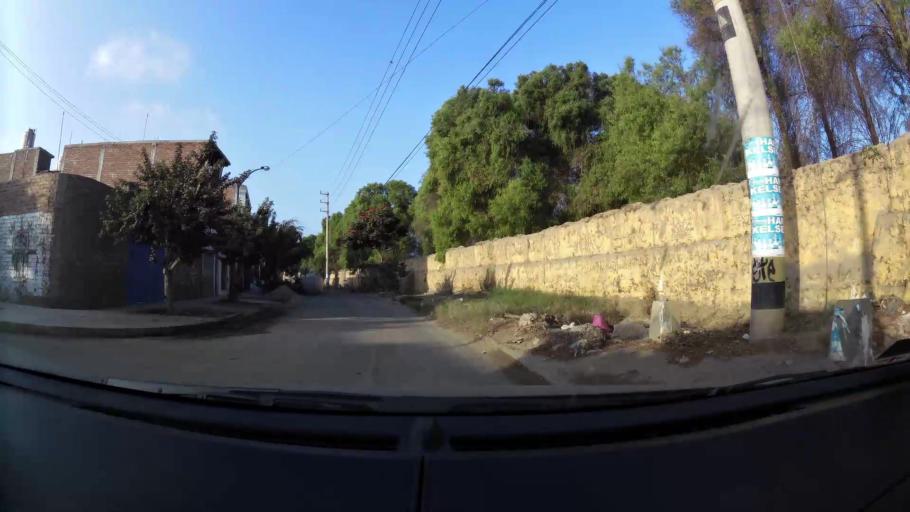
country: PE
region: La Libertad
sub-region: Provincia de Trujillo
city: El Porvenir
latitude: -8.0929
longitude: -78.9942
